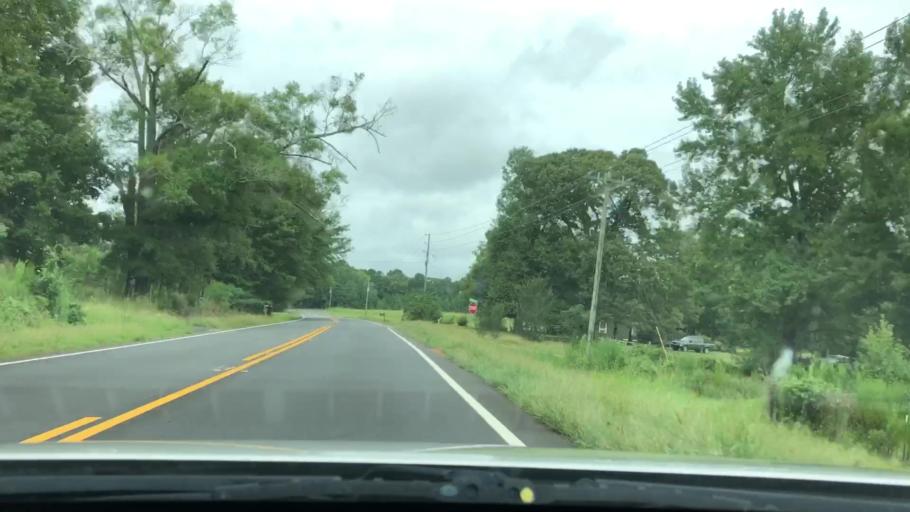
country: US
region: Georgia
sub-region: Upson County
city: Hannahs Mill
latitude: 33.0148
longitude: -84.4415
